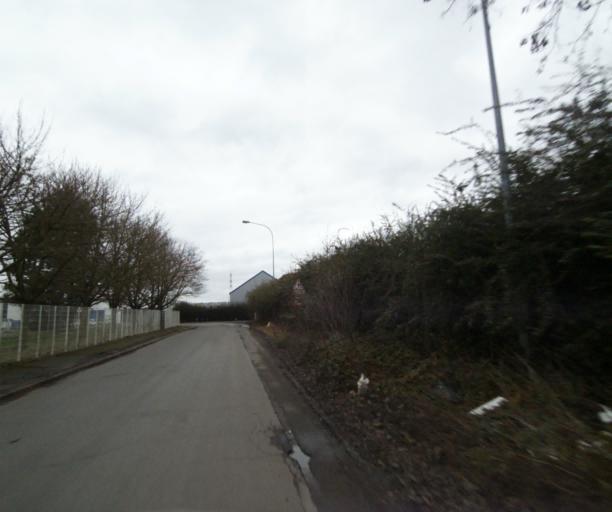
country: FR
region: Nord-Pas-de-Calais
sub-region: Departement du Nord
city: Anzin
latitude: 50.3787
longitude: 3.5242
